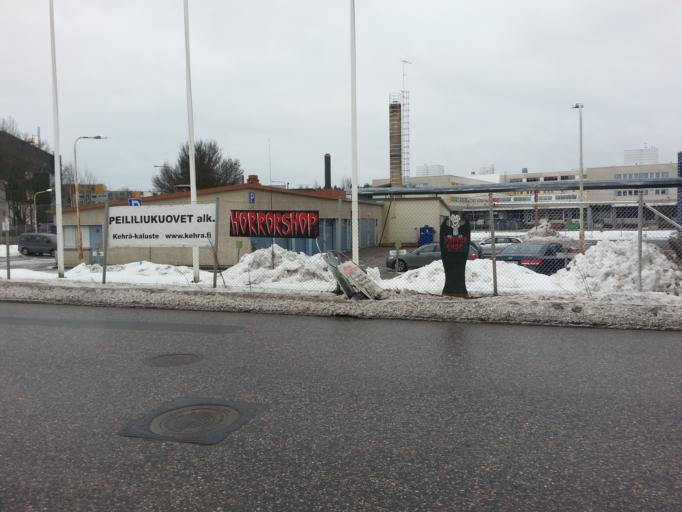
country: FI
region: Uusimaa
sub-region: Helsinki
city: Teekkarikylae
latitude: 60.2414
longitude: 24.8467
